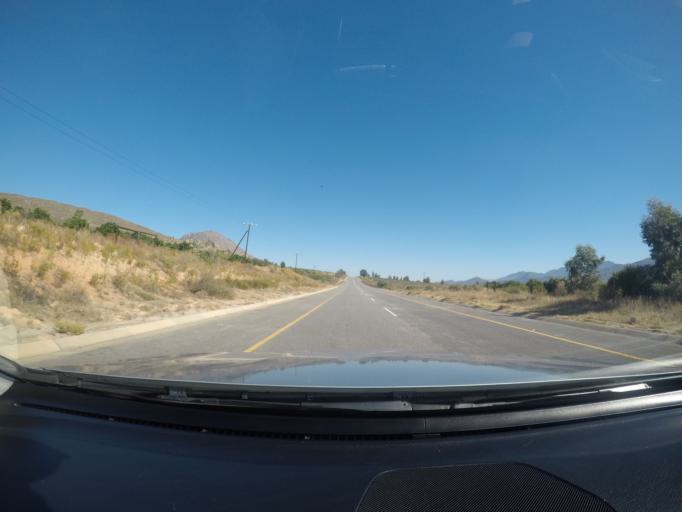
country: ZA
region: Western Cape
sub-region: West Coast District Municipality
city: Clanwilliam
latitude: -32.5468
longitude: 18.9799
